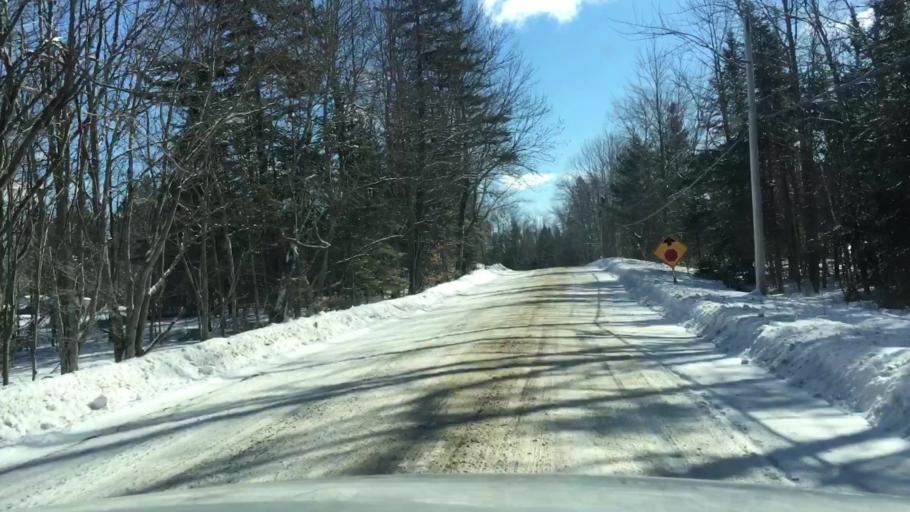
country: US
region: Maine
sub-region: Washington County
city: Calais
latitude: 45.0702
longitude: -67.4771
